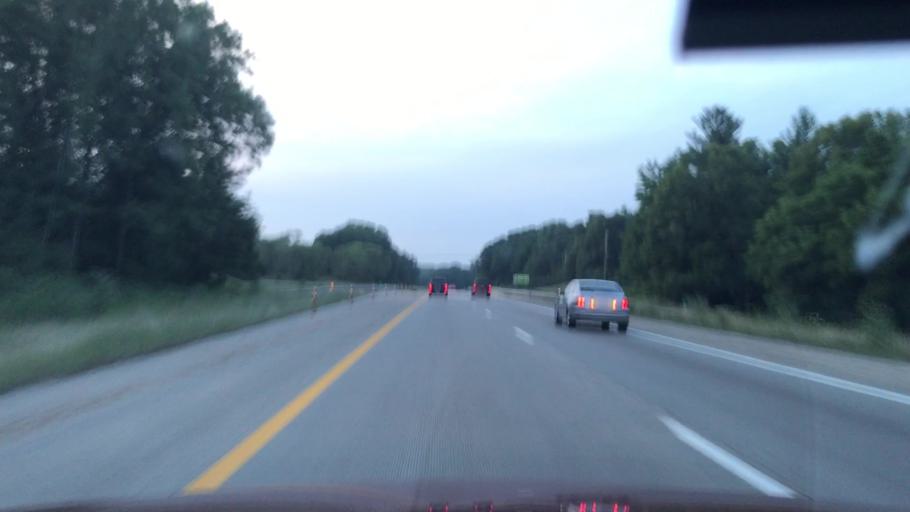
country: US
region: Michigan
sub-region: Kent County
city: Comstock Park
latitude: 43.0567
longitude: -85.6627
